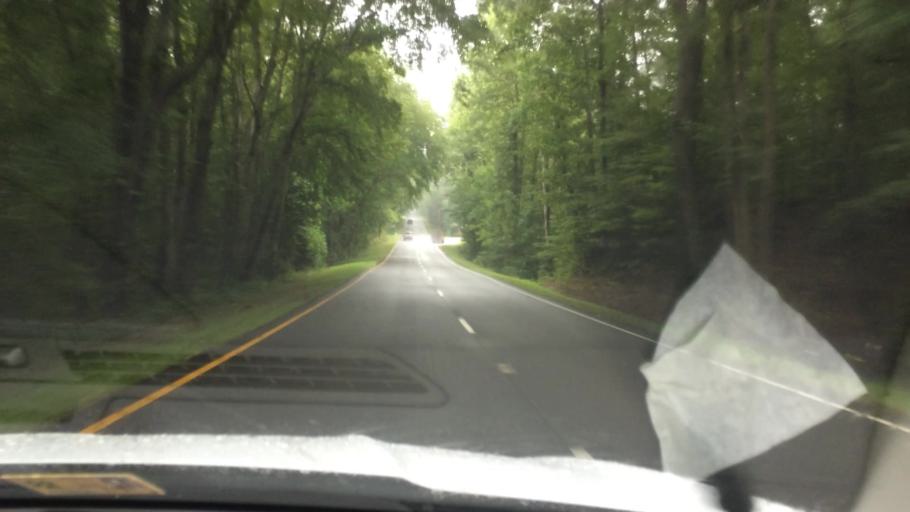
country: US
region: Virginia
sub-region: James City County
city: Williamsburg
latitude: 37.3960
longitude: -76.7847
